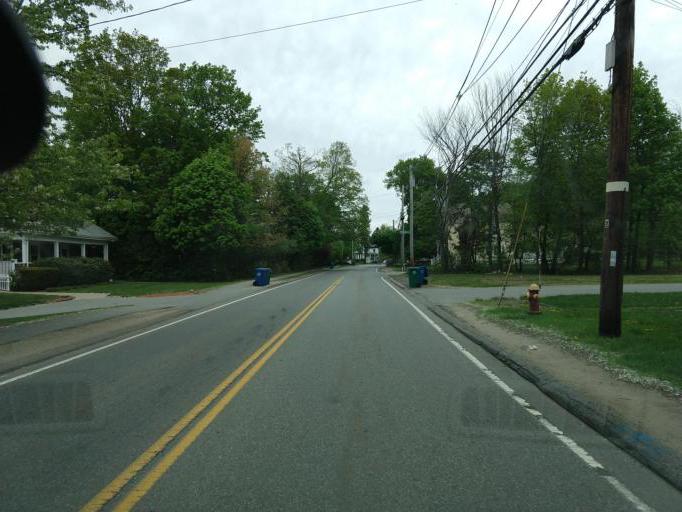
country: US
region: Massachusetts
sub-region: Middlesex County
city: Billerica
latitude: 42.5619
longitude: -71.2654
